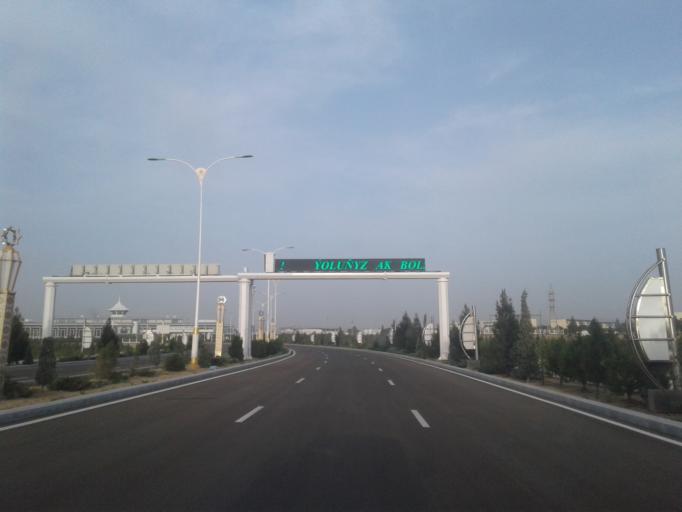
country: TM
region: Balkan
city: Turkmenbasy
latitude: 40.0436
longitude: 52.9856
